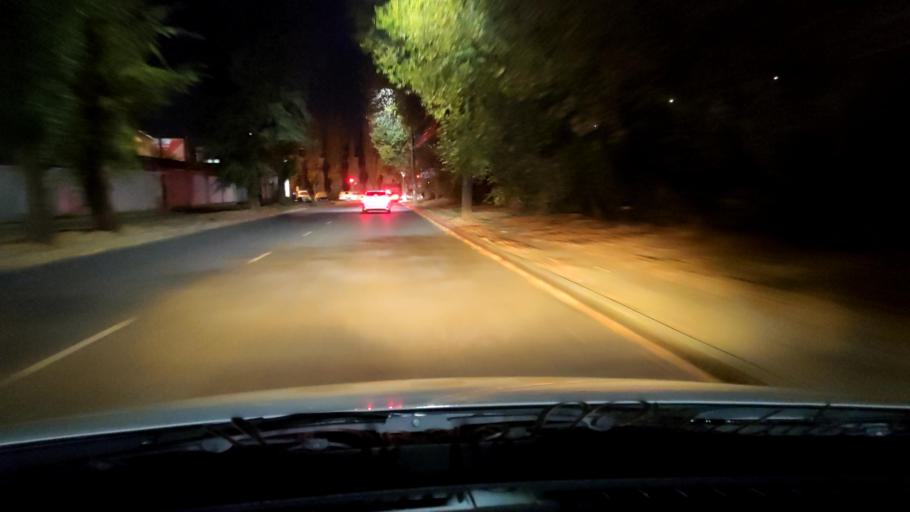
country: RU
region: Voronezj
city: Voronezh
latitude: 51.6875
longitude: 39.1673
